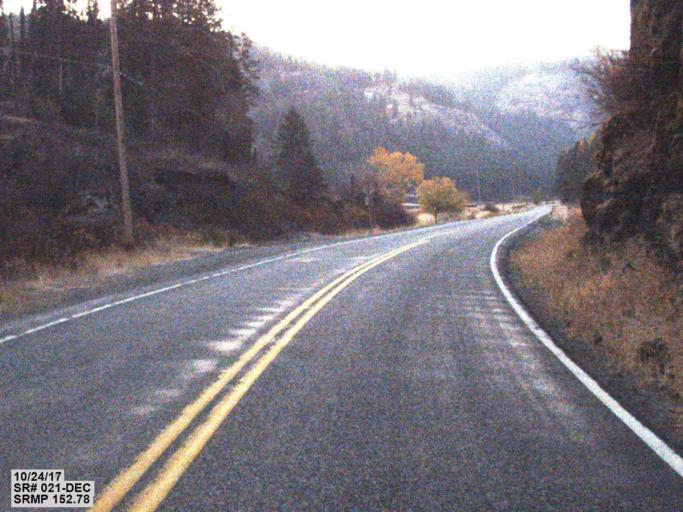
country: US
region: Washington
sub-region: Ferry County
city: Republic
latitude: 48.5417
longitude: -118.7455
